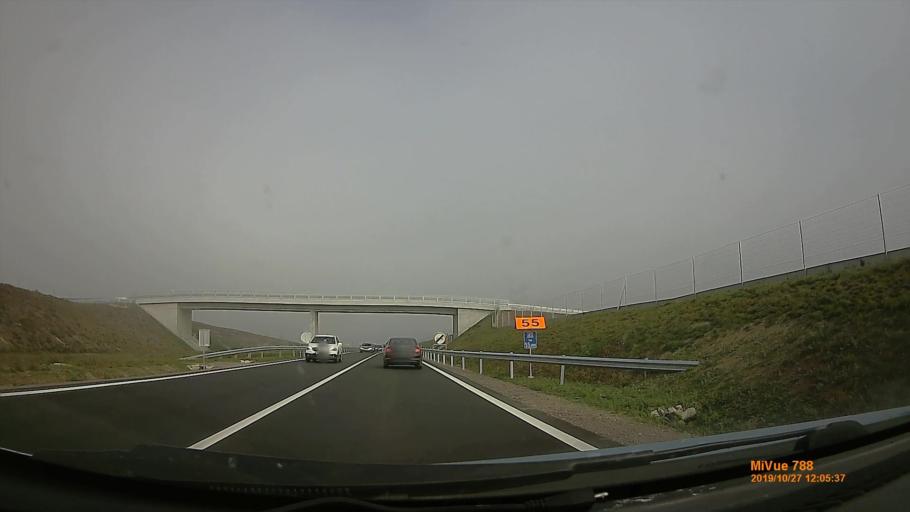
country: AT
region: Lower Austria
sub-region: Politischer Bezirk Mistelbach
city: Drasenhofen
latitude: 48.7655
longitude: 16.6379
